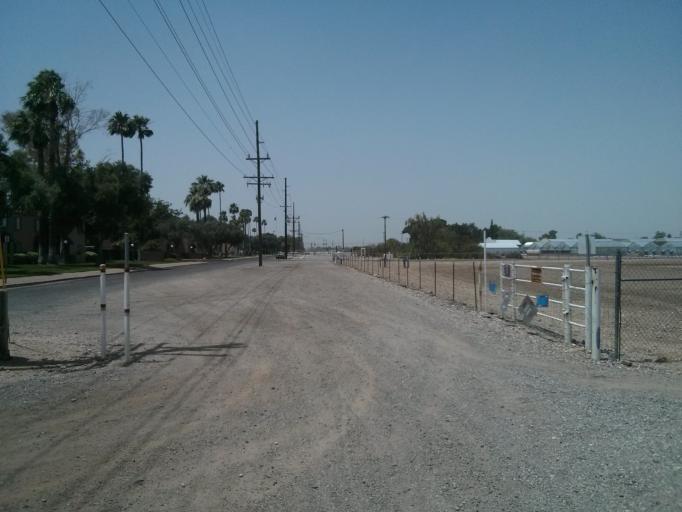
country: US
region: Arizona
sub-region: Pima County
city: Catalina Foothills
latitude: 32.2795
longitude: -110.9395
